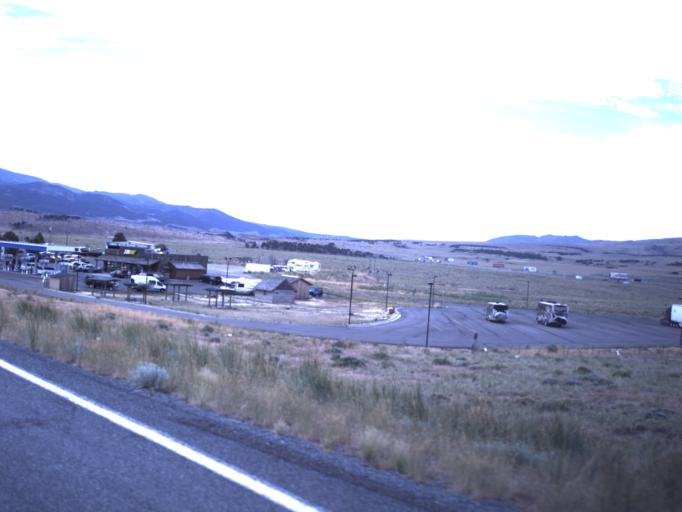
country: US
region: Utah
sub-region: Beaver County
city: Beaver
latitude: 38.6147
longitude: -112.6059
